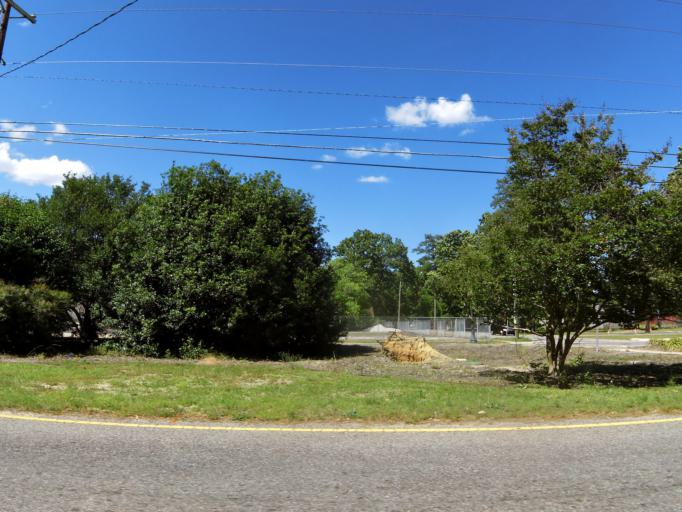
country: US
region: South Carolina
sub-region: Aiken County
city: Aiken
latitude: 33.5571
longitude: -81.7089
